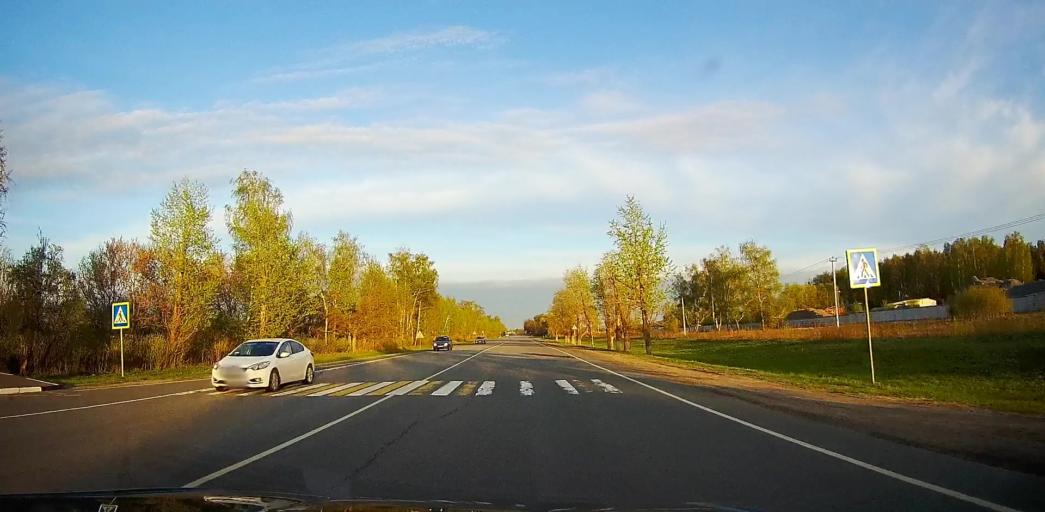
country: RU
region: Moskovskaya
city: Troitskoye
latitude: 55.2157
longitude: 38.5929
